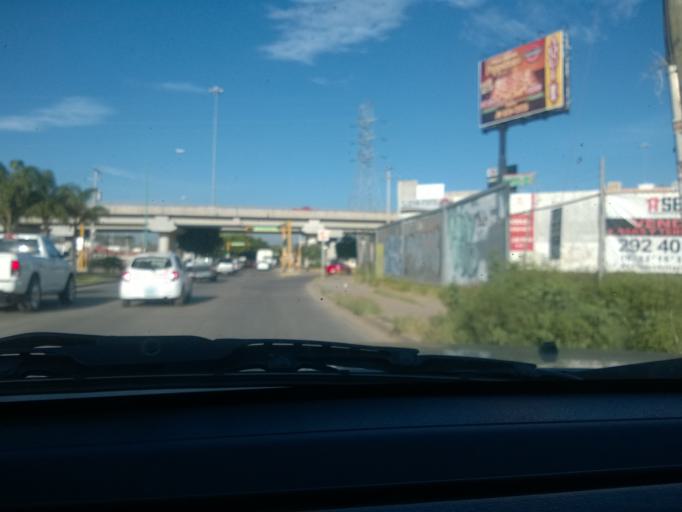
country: MX
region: Guanajuato
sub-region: Leon
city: Medina
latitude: 21.1251
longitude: -101.6275
